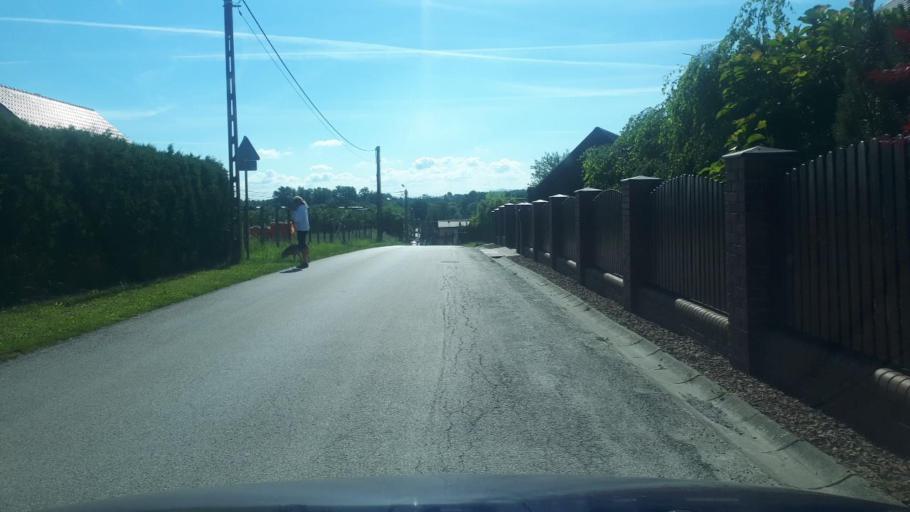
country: PL
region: Silesian Voivodeship
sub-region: Powiat bielski
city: Pisarzowice
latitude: 49.8761
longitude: 19.1304
